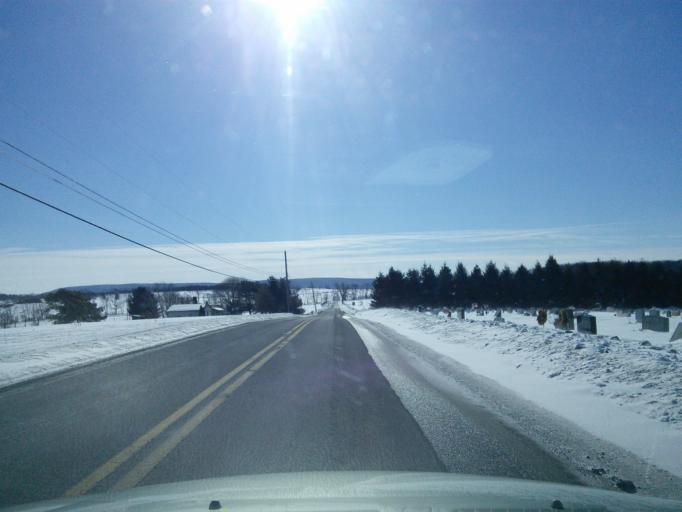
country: US
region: Pennsylvania
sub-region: Centre County
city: Houserville
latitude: 40.8738
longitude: -77.8464
